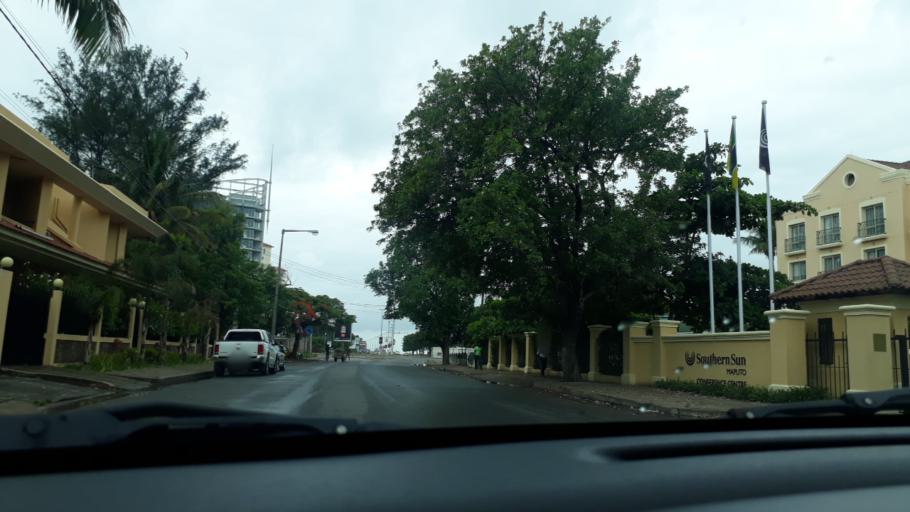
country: MZ
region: Maputo City
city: Maputo
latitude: -25.9597
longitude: 32.6049
